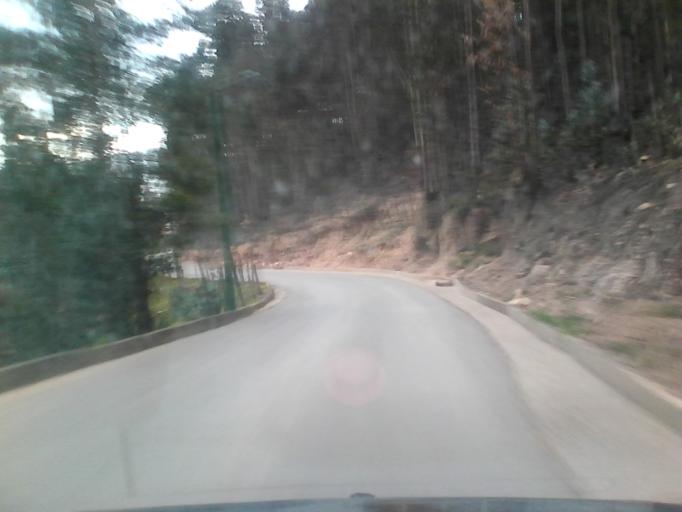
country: CO
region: Boyaca
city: Duitama
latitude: 5.8470
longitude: -73.0378
